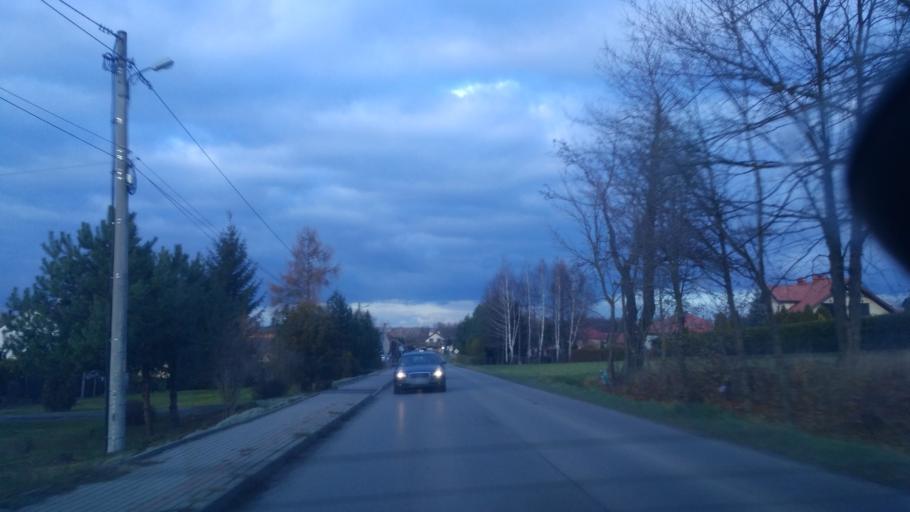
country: PL
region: Subcarpathian Voivodeship
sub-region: Powiat rzeszowski
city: Krasne
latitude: 50.0649
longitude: 22.1194
